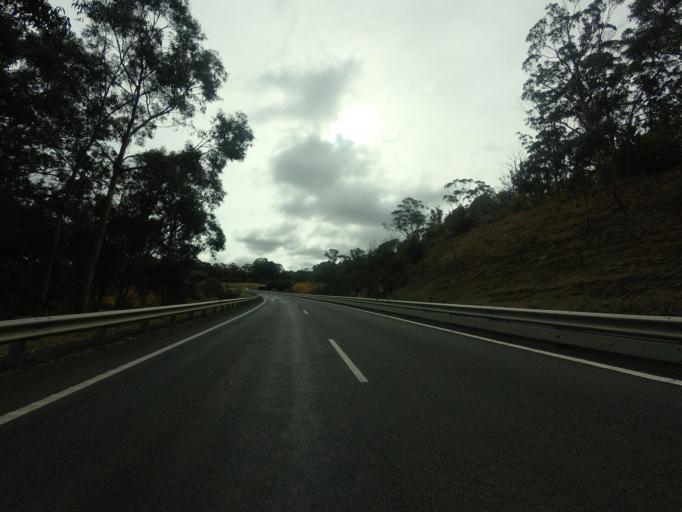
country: AU
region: Tasmania
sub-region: Brighton
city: Bridgewater
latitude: -42.5798
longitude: 147.2287
